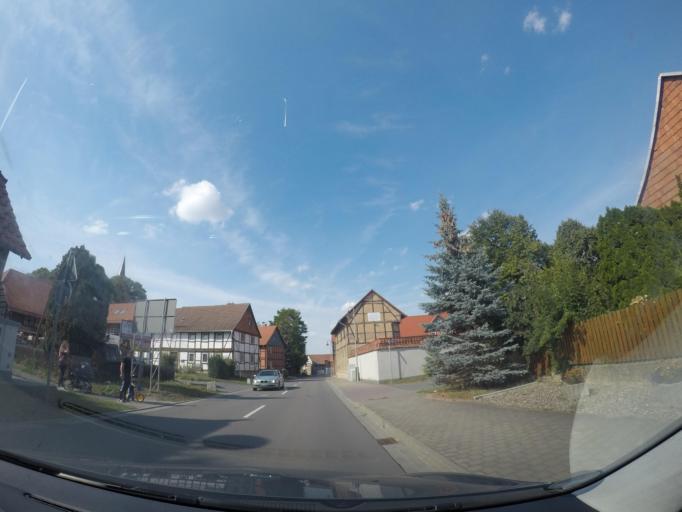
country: DE
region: Saxony-Anhalt
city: Langeln
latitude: 51.9095
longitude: 10.7956
